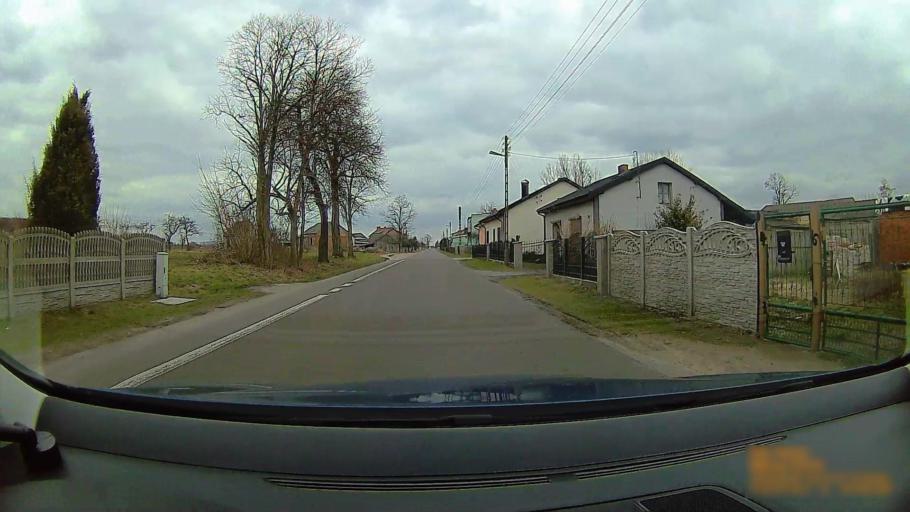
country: PL
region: Greater Poland Voivodeship
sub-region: Powiat koninski
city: Rzgow Pierwszy
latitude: 52.1217
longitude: 18.0676
